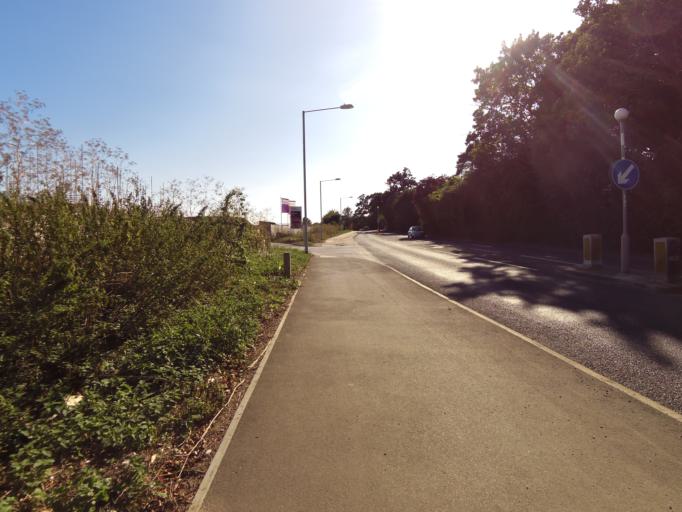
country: GB
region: England
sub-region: Essex
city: Witham
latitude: 51.7895
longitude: 0.6248
